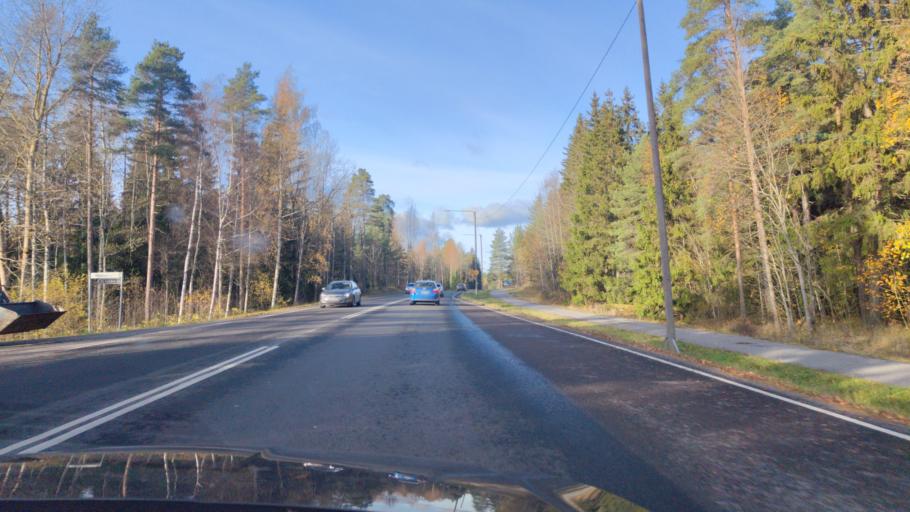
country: FI
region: Varsinais-Suomi
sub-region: Turku
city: Kaarina
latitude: 60.4554
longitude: 22.3676
